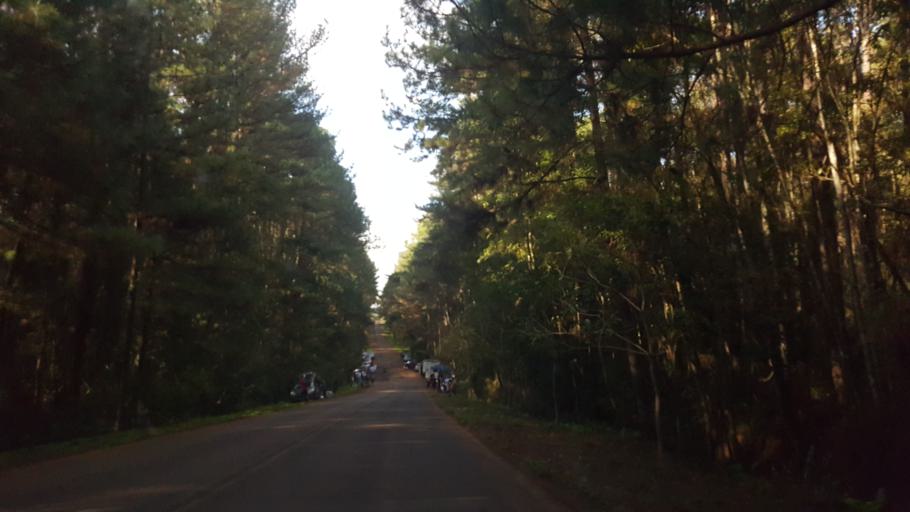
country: AR
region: Misiones
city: Puerto Leoni
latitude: -27.0053
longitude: -55.1894
